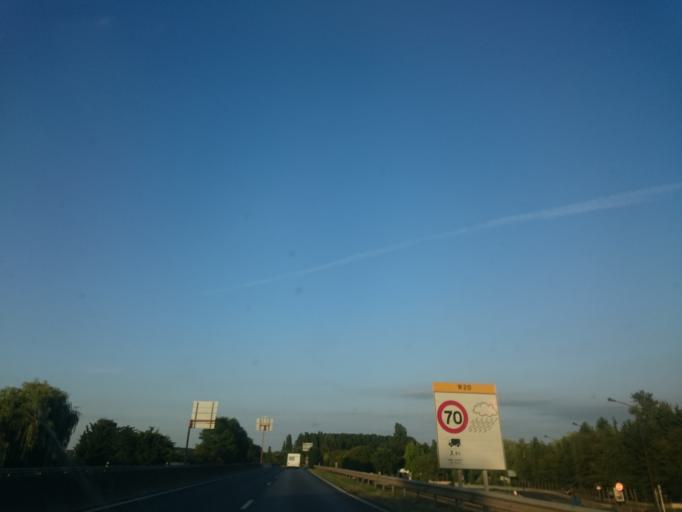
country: FR
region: Ile-de-France
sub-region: Departement de l'Essonne
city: Etampes
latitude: 48.4281
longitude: 2.1569
